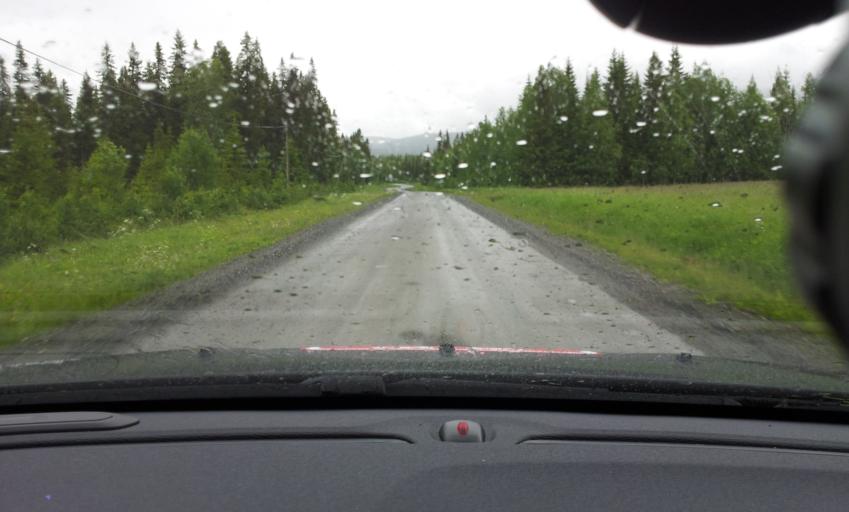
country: SE
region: Jaemtland
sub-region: Are Kommun
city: Are
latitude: 63.4400
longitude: 12.8076
